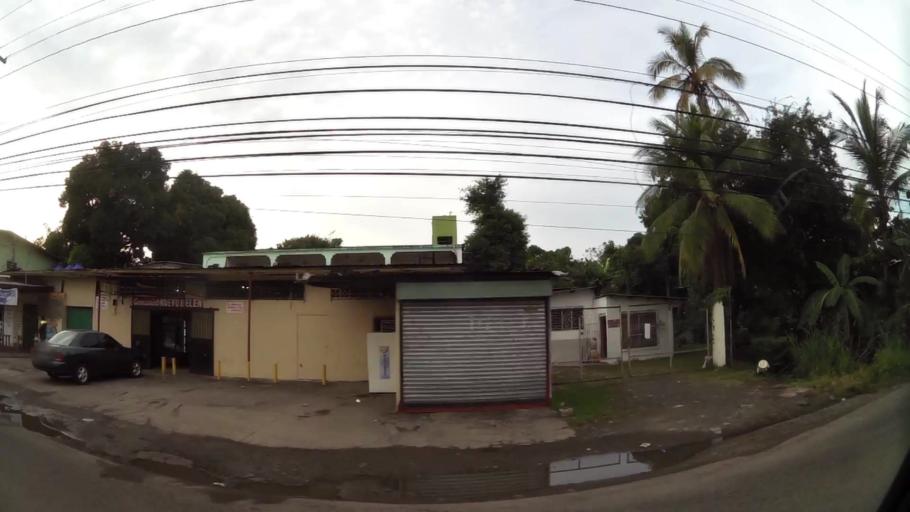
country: PA
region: Panama
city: Tocumen
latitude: 9.0846
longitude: -79.3931
